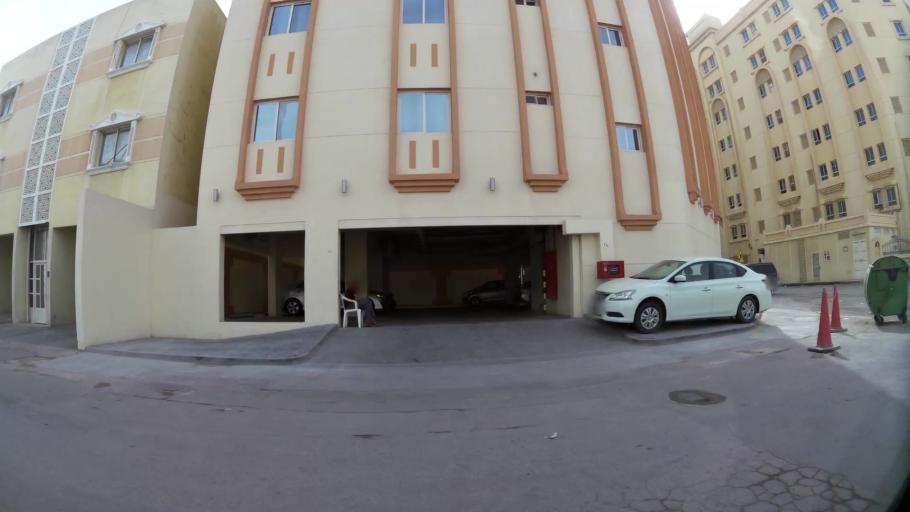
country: QA
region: Baladiyat ad Dawhah
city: Doha
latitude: 25.2801
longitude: 51.5498
